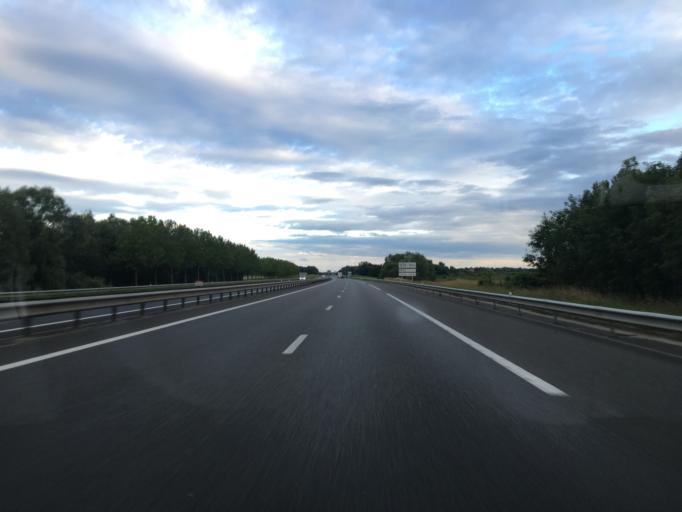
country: FR
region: Ile-de-France
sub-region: Departement de Seine-et-Marne
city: Moissy-Cramayel
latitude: 48.6246
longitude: 2.6292
